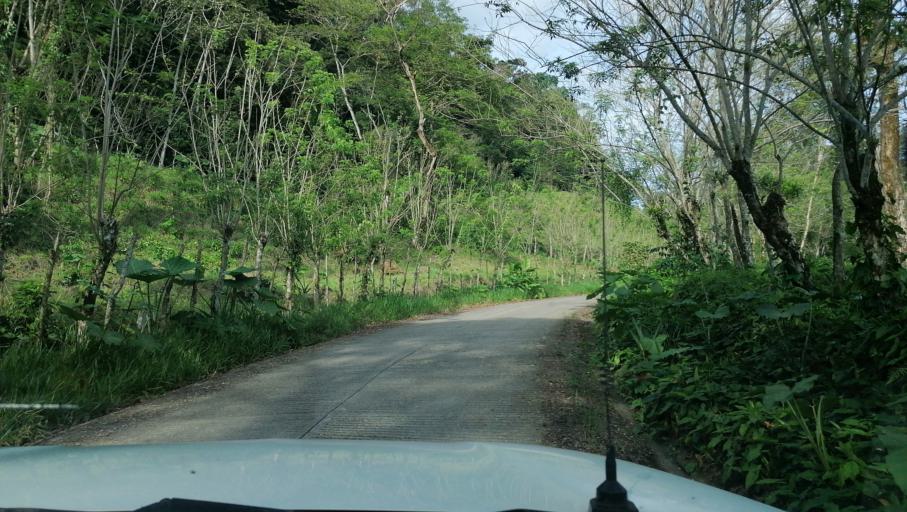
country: MX
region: Chiapas
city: Ostuacan
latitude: 17.4756
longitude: -93.2394
